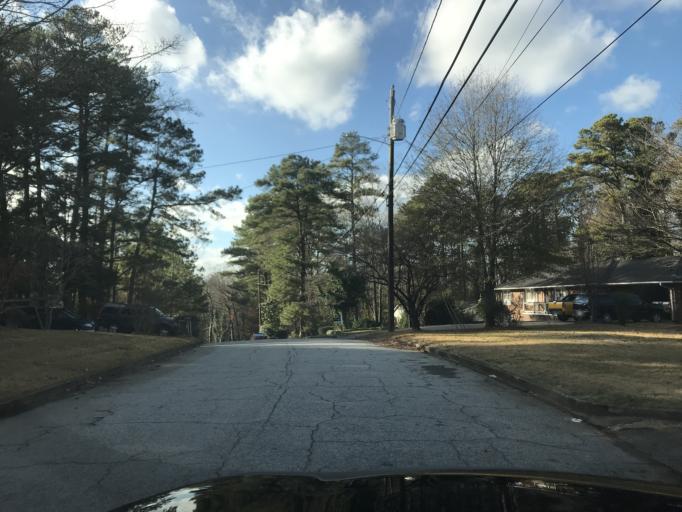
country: US
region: Georgia
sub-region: Fulton County
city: College Park
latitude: 33.6364
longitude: -84.4751
